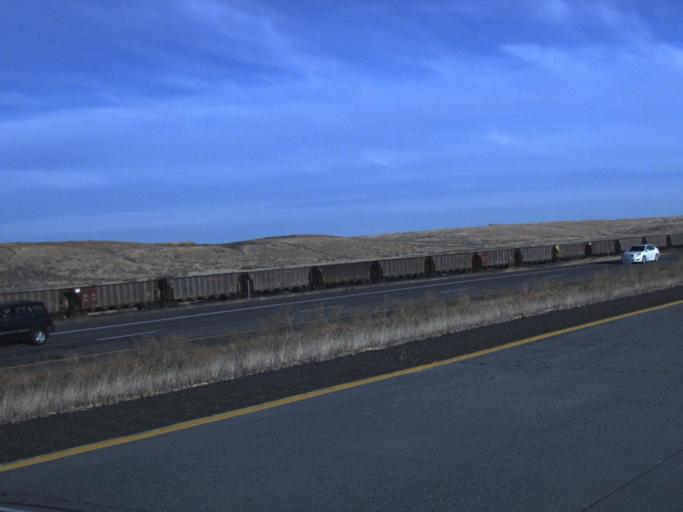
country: US
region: Washington
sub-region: Franklin County
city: Basin City
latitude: 46.4988
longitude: -119.0151
